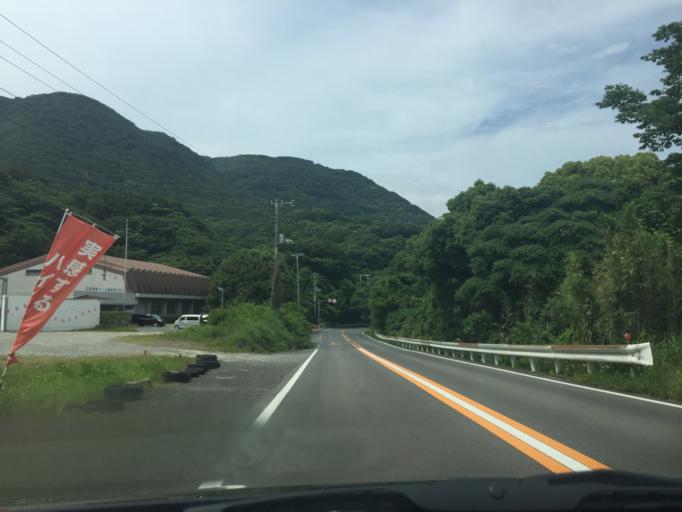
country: JP
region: Shizuoka
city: Shimoda
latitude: 34.7287
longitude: 138.9915
